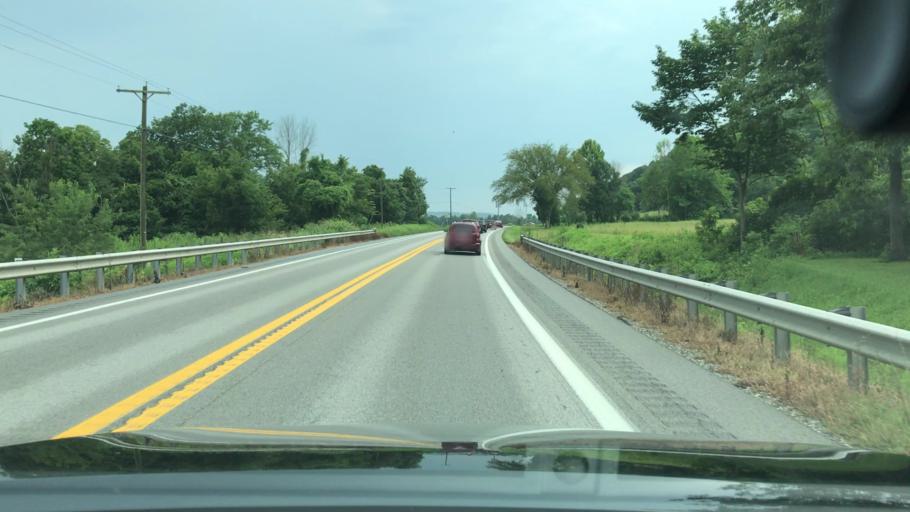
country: US
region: West Virginia
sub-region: Putnam County
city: Buffalo
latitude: 38.6522
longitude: -81.9703
